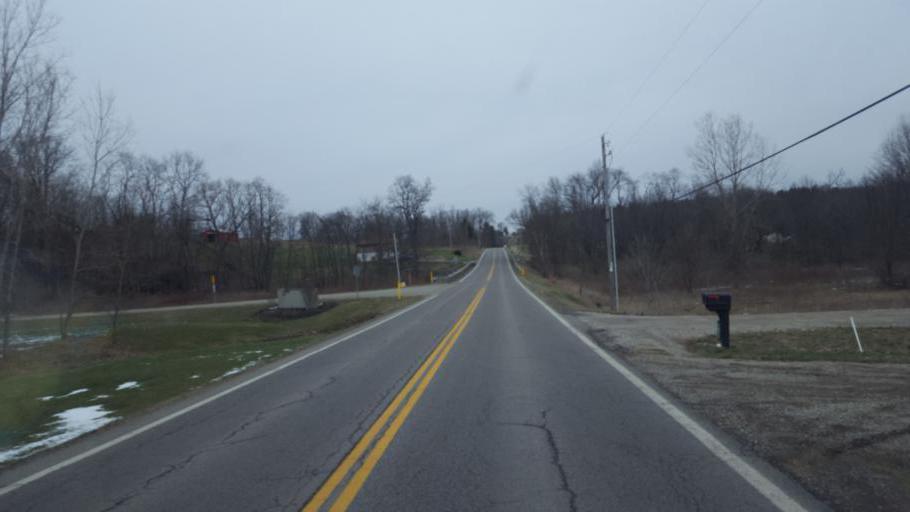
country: US
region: Ohio
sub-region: Richland County
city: Lexington
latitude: 40.6616
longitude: -82.5887
